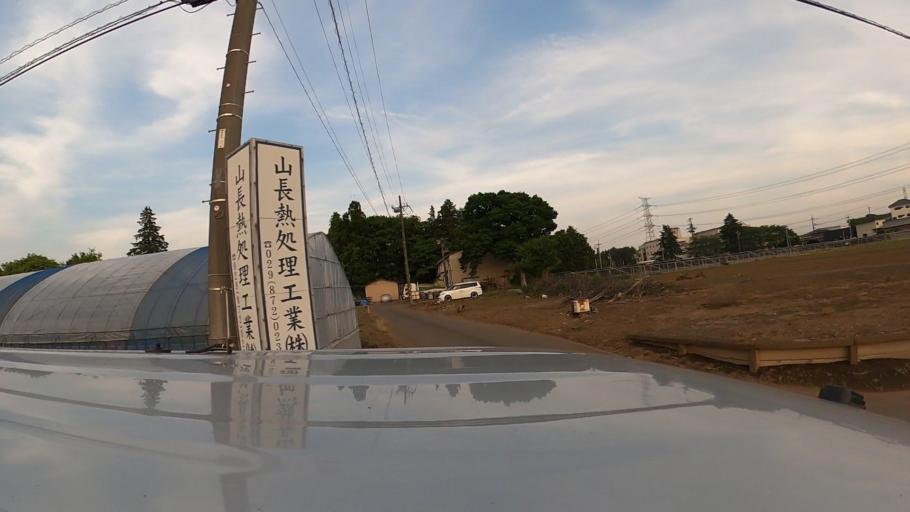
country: JP
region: Ibaraki
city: Ushiku
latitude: 36.0077
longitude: 140.1226
